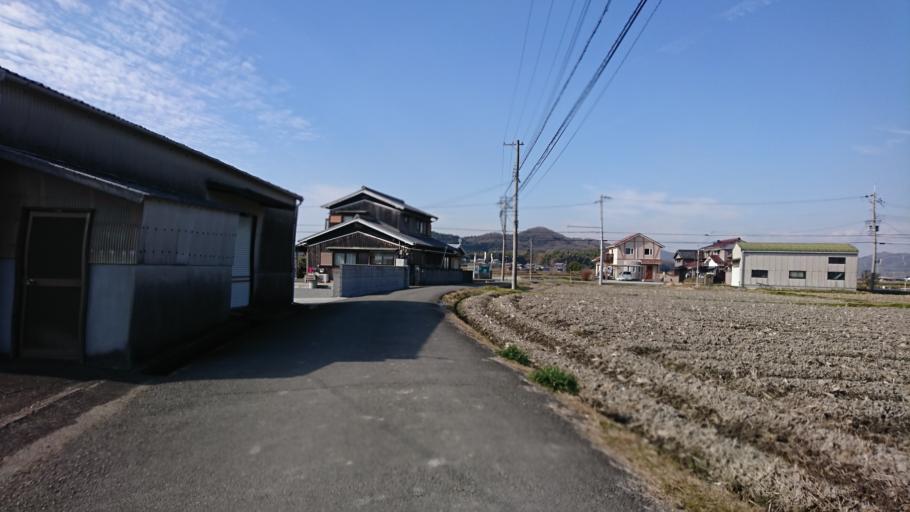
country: JP
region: Hyogo
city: Kakogawacho-honmachi
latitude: 34.8151
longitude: 134.8550
